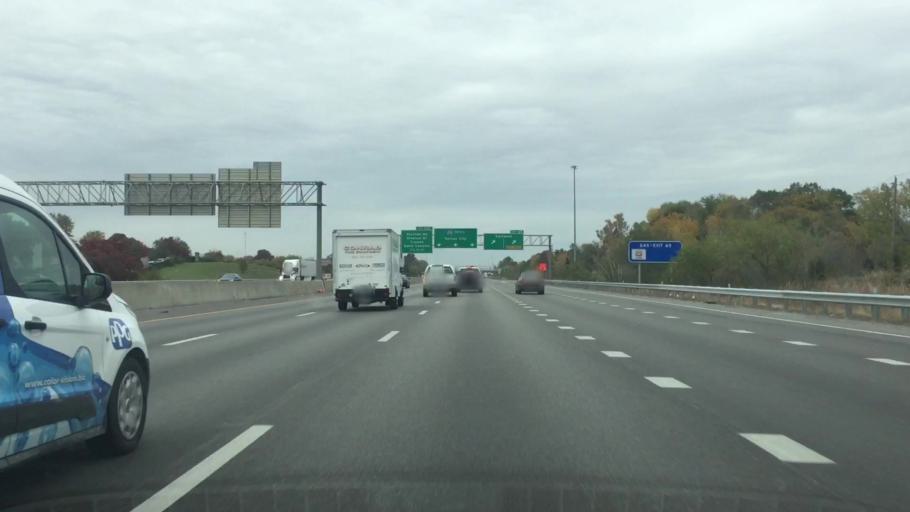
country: US
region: Missouri
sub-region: Jackson County
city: Raytown
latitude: 39.0260
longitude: -94.5007
